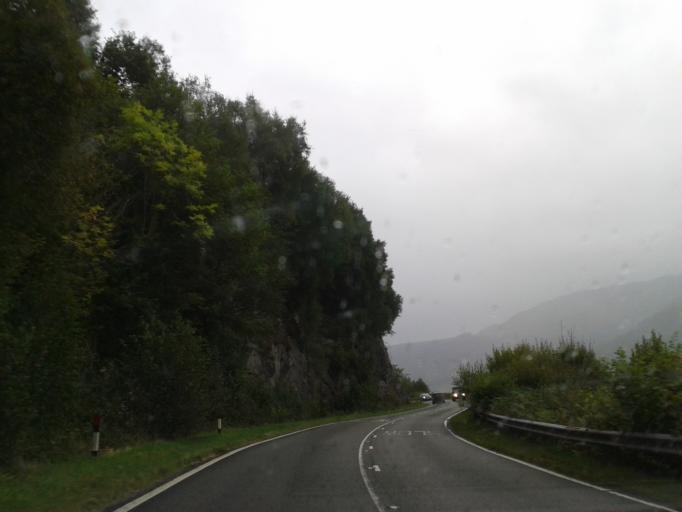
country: GB
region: Scotland
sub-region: Highland
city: Fort William
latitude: 57.2667
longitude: -5.5044
